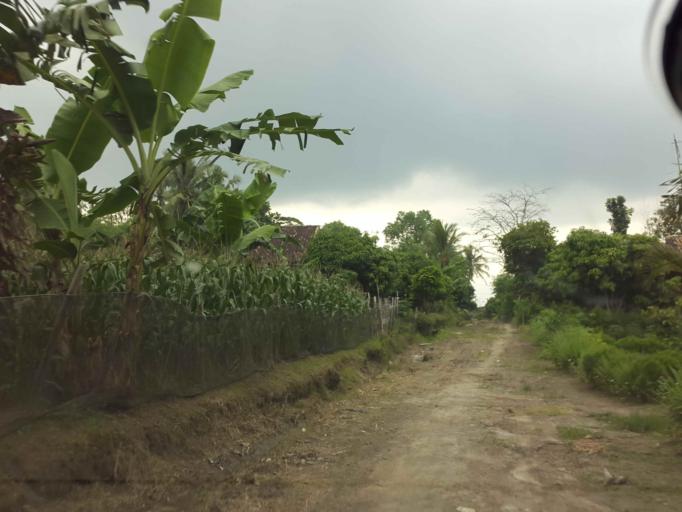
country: ID
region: Lampung
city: Palas
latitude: -5.6217
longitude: 105.6354
